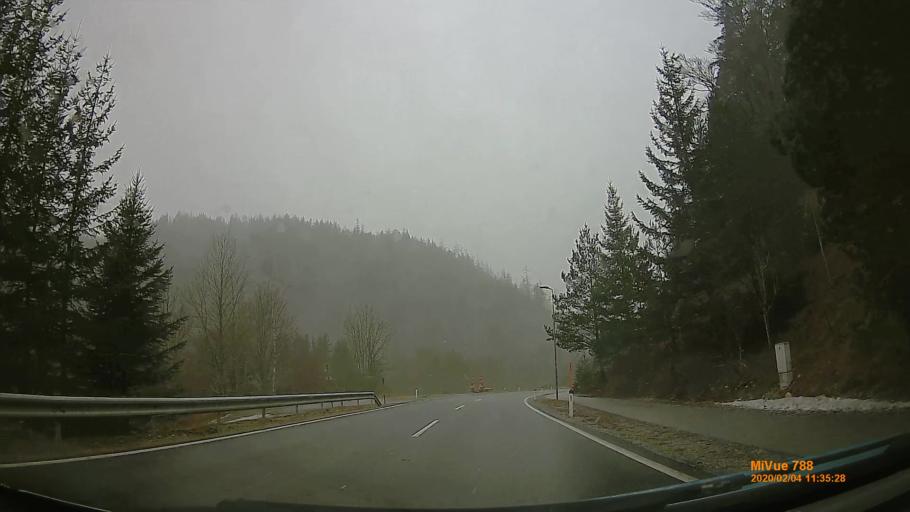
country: AT
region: Styria
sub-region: Politischer Bezirk Bruck-Muerzzuschlag
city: Neuberg an der Muerz
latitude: 47.6732
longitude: 15.5618
